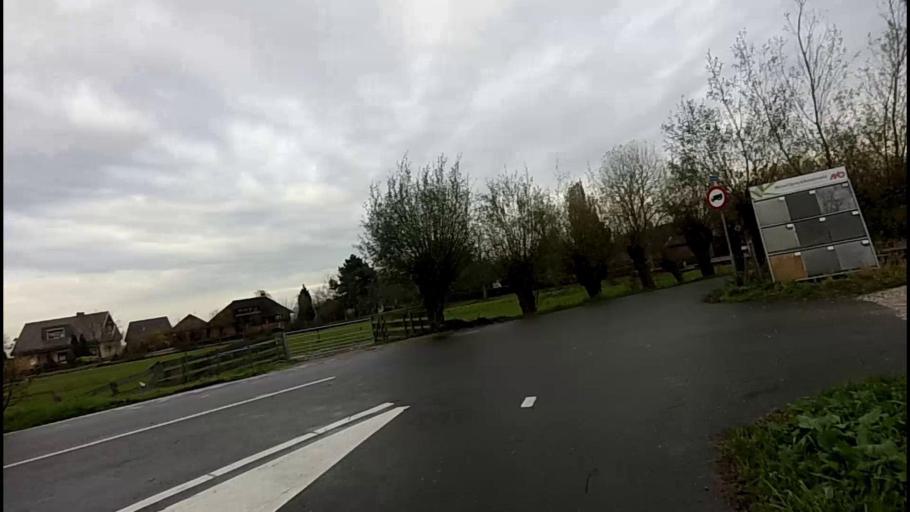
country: NL
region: South Holland
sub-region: Gemeente Alblasserdam
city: Alblasserdam
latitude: 51.8975
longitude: 4.6408
